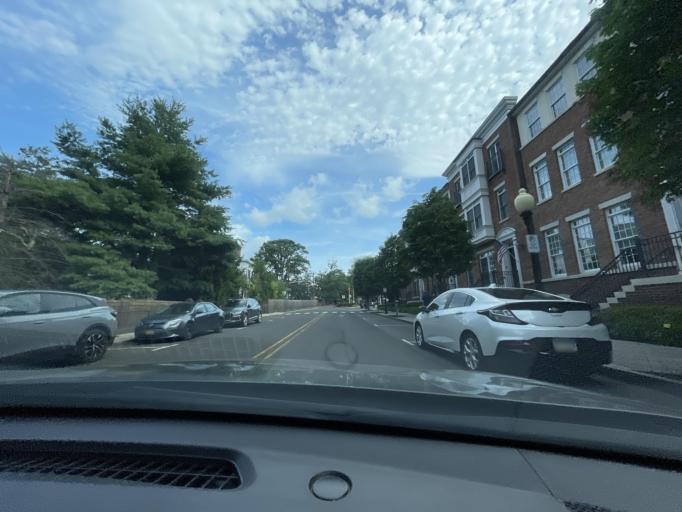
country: US
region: New Jersey
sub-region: Mercer County
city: Princeton
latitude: 40.3510
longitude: -74.6632
